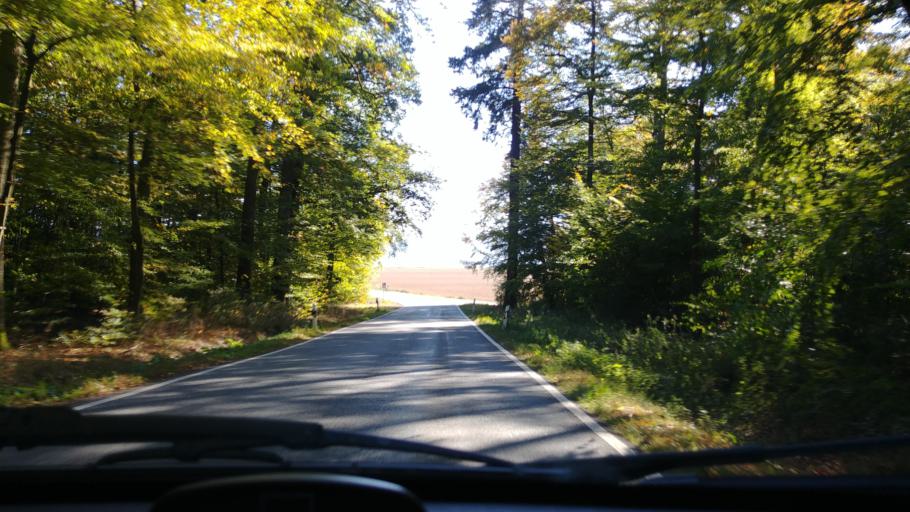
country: DE
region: Hesse
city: Taunusstein
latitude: 50.1493
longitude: 8.1230
